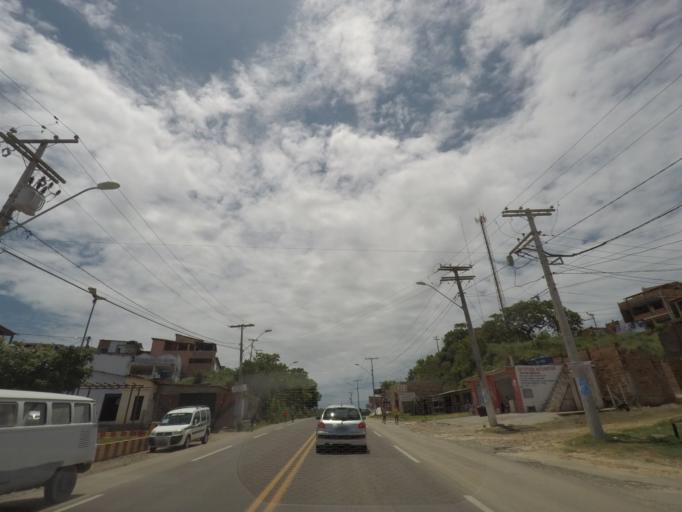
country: BR
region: Bahia
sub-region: Itaparica
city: Itaparica
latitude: -12.9337
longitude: -38.6236
